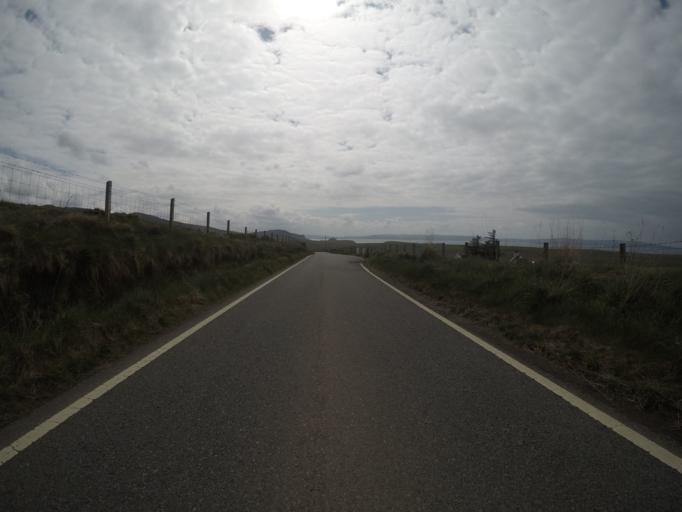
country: GB
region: Scotland
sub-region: Highland
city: Portree
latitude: 57.6314
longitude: -6.3780
